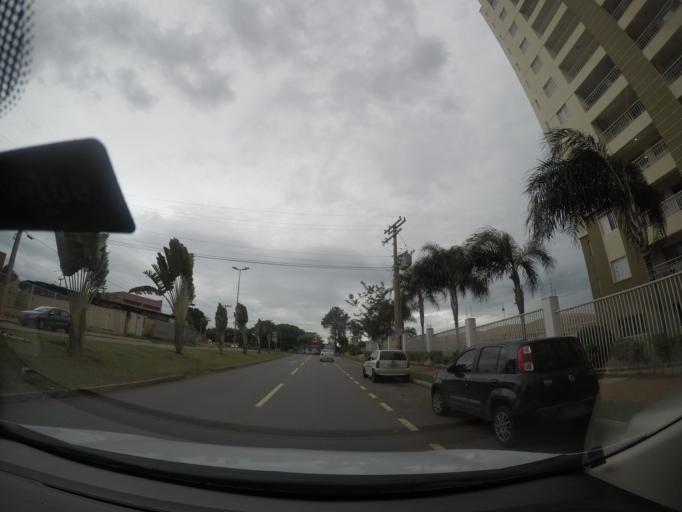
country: BR
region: Goias
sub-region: Goiania
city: Goiania
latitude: -16.7118
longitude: -49.3175
